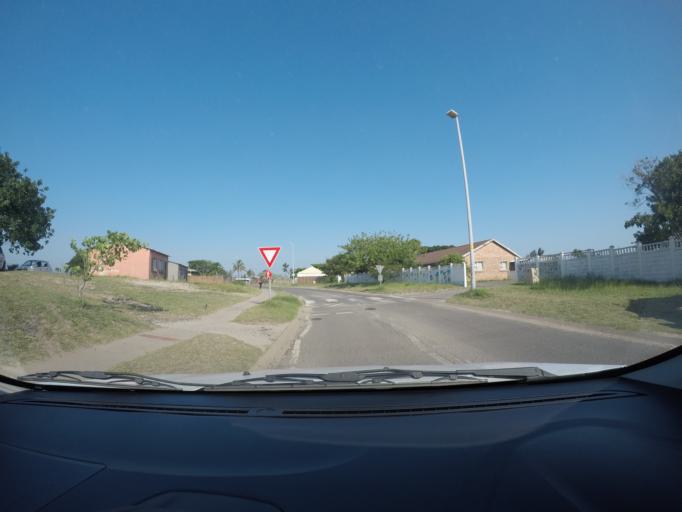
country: ZA
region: KwaZulu-Natal
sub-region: uThungulu District Municipality
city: Richards Bay
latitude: -28.7155
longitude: 32.0345
